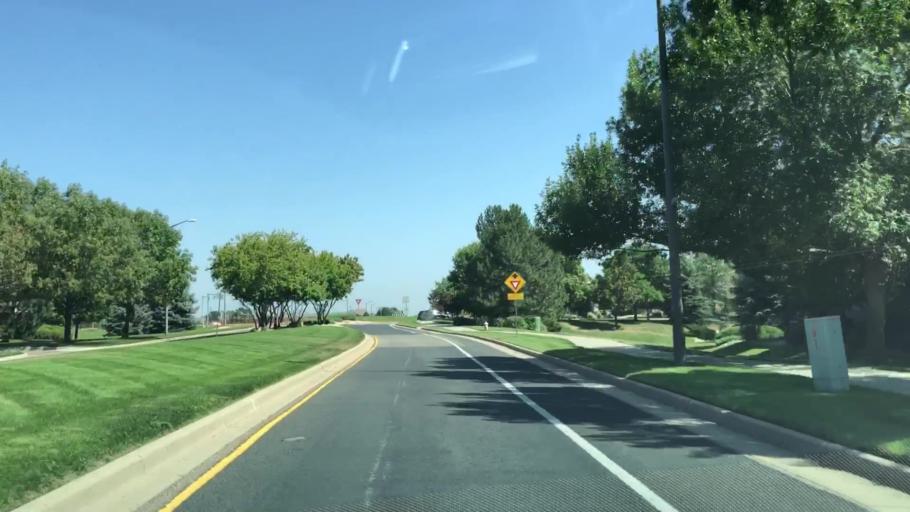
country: US
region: Colorado
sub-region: Larimer County
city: Loveland
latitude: 40.4104
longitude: -105.0039
